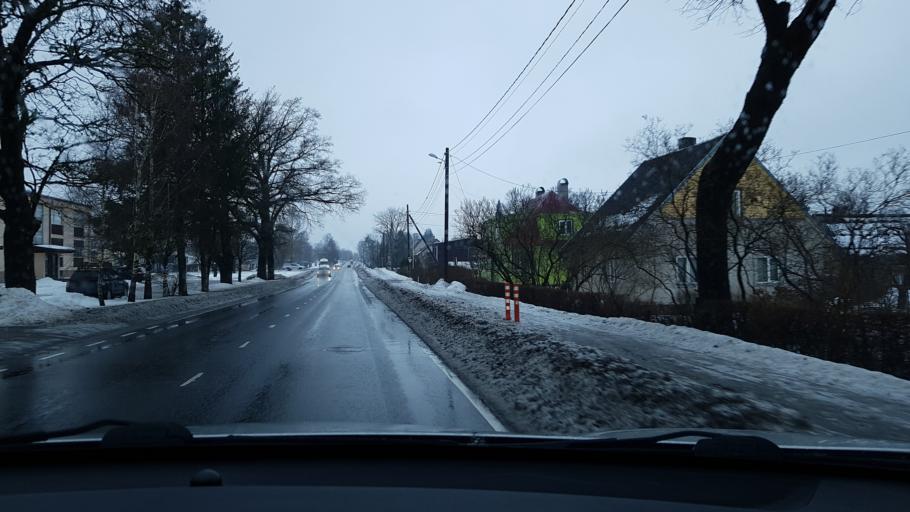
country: EE
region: Jaervamaa
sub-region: Tueri vald
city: Tueri
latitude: 58.8104
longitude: 25.4132
